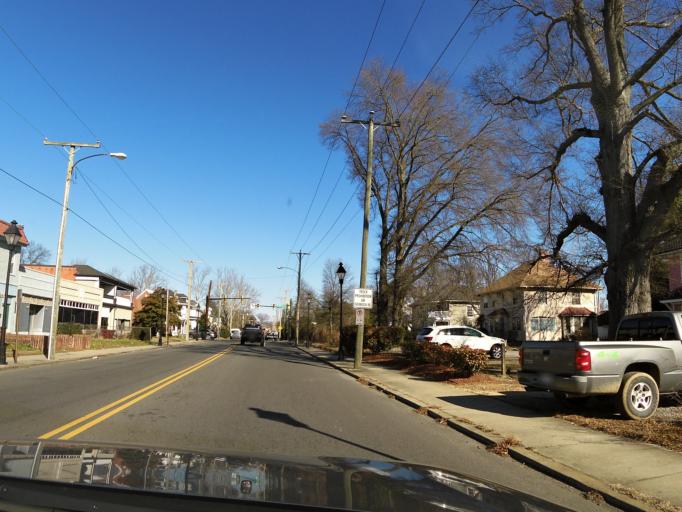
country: US
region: Virginia
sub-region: City of Richmond
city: Richmond
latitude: 37.5643
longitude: -77.4332
